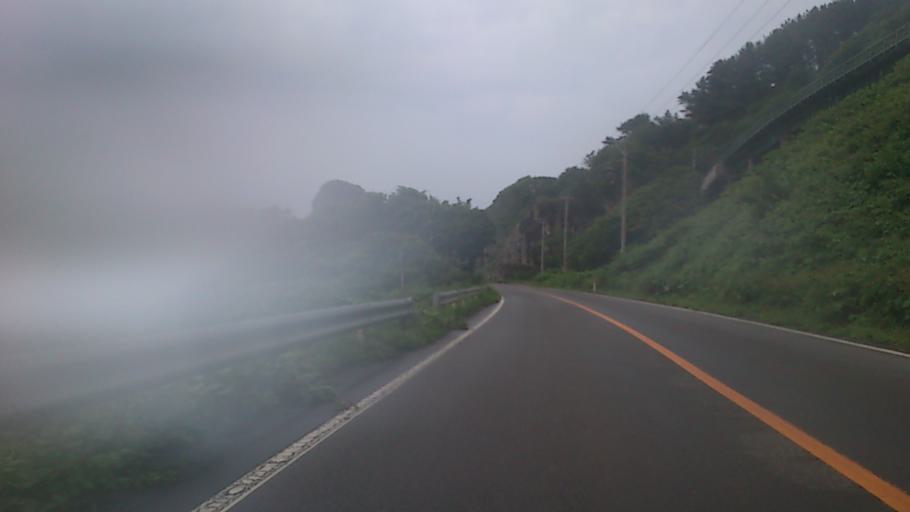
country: JP
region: Akita
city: Noshiromachi
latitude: 40.4437
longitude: 139.9402
